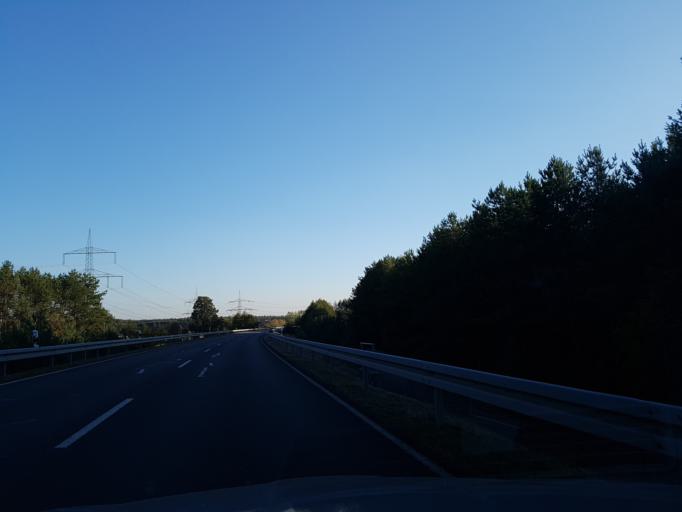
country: DE
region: Brandenburg
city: Bad Liebenwerda
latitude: 51.5204
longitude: 13.4248
